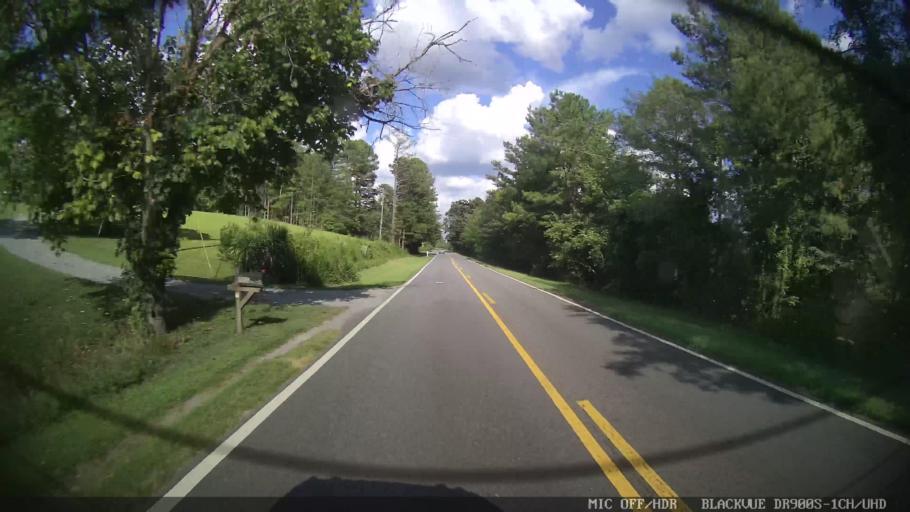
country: US
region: Georgia
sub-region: Bartow County
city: Euharlee
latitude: 34.1769
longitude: -85.0008
